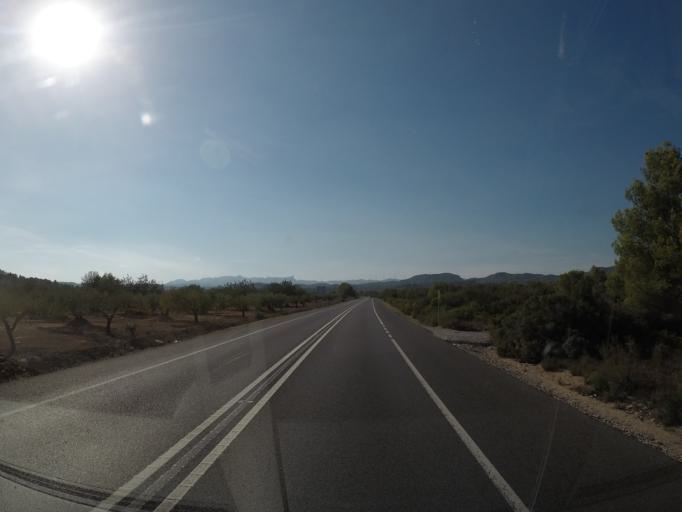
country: ES
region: Catalonia
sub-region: Provincia de Tarragona
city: El Perello
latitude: 40.8969
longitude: 0.7413
